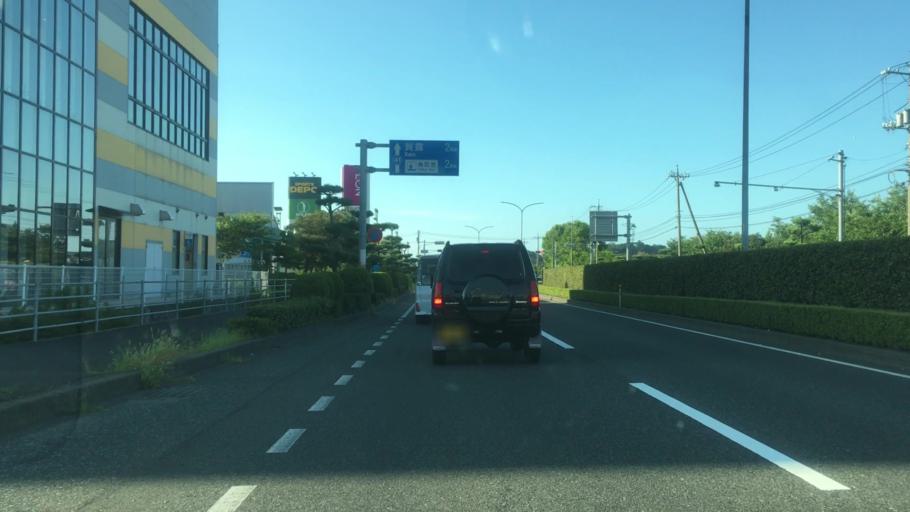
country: JP
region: Tottori
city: Tottori
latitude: 35.5213
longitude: 134.2025
